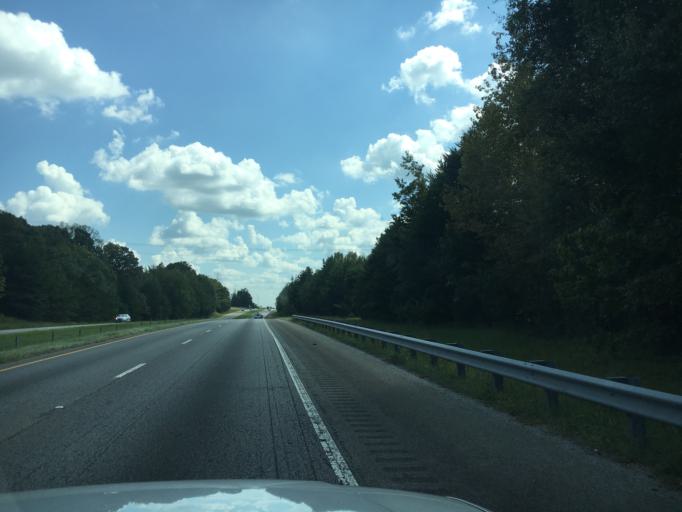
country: US
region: South Carolina
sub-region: Spartanburg County
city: Roebuck
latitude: 34.8595
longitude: -81.9812
